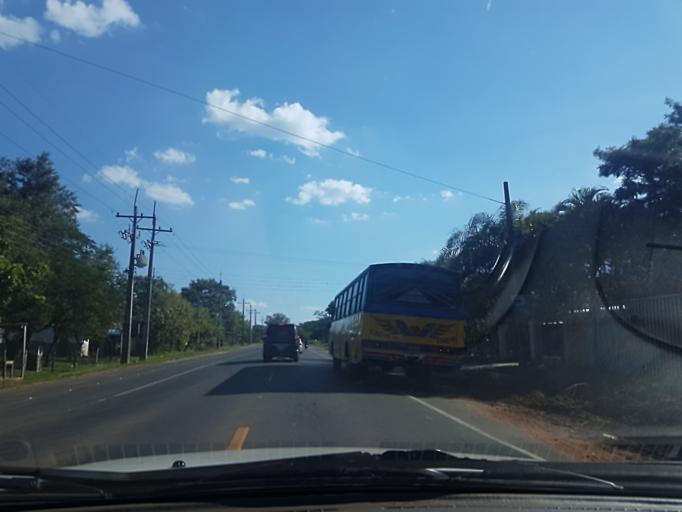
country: PY
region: Central
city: Aregua
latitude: -25.2351
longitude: -57.4210
